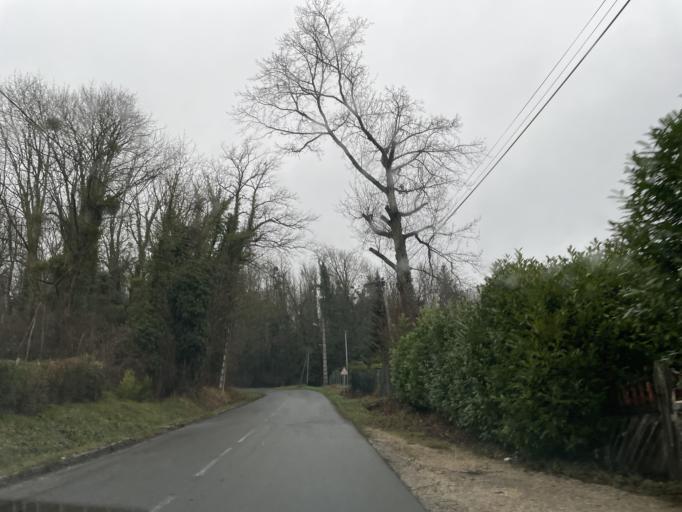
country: FR
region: Ile-de-France
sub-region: Departement de Seine-et-Marne
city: Pommeuse
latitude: 48.8202
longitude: 3.0105
